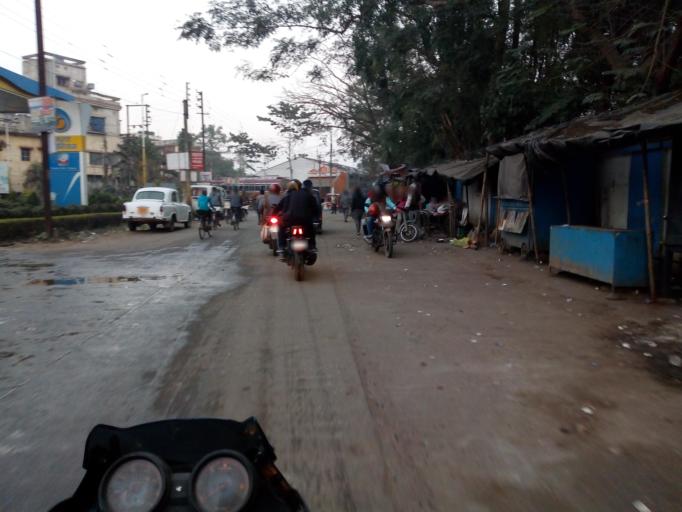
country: IN
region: West Bengal
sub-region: Bankura
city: Bankura
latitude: 23.2392
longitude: 87.0339
